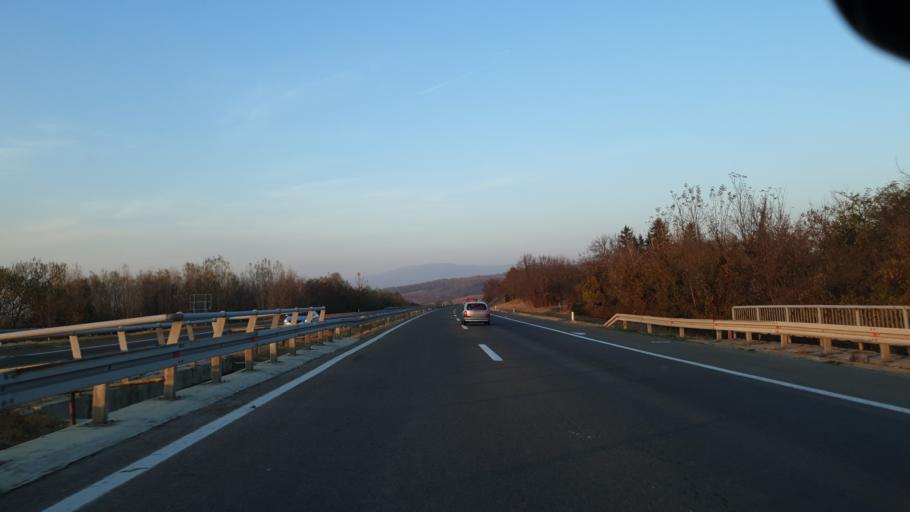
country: RS
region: Central Serbia
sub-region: Nisavski Okrug
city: Nis
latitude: 43.4242
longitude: 21.7966
